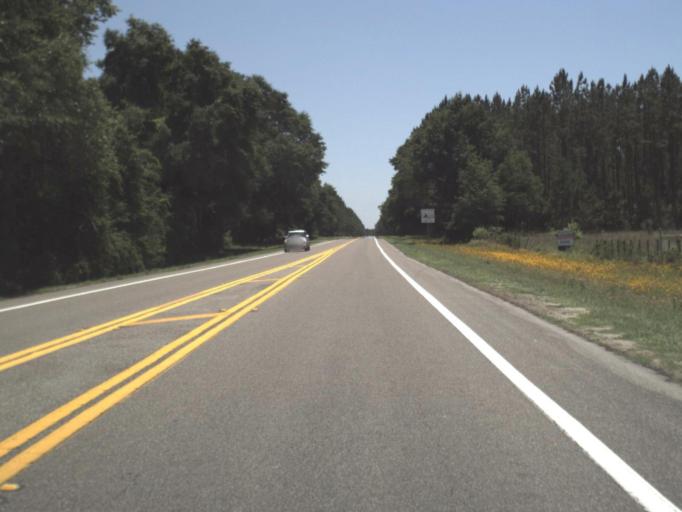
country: US
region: Florida
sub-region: Suwannee County
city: Wellborn
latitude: 30.2206
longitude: -82.8215
